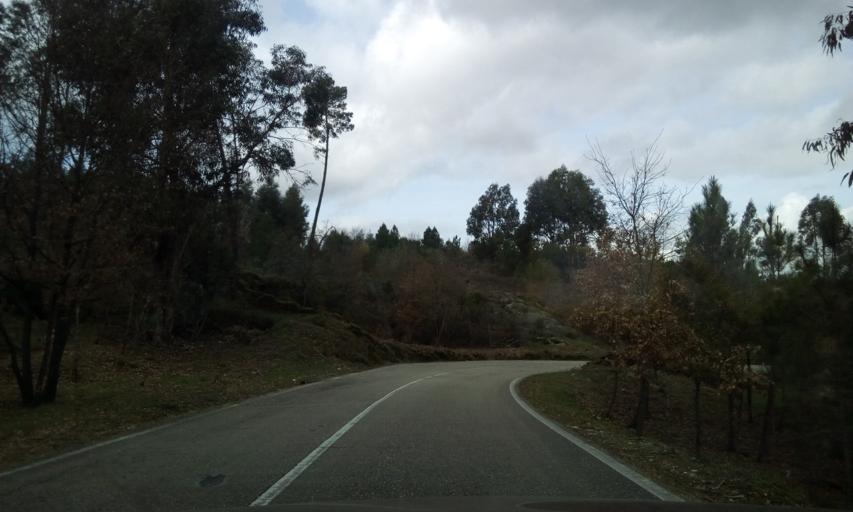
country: PT
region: Viseu
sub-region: Satao
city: Satao
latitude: 40.6604
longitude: -7.6646
